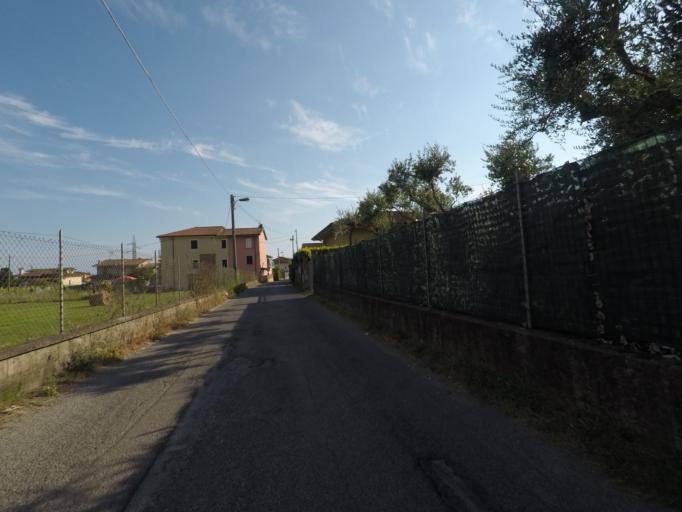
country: IT
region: Tuscany
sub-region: Provincia di Massa-Carrara
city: Massa
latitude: 44.0160
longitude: 10.1414
